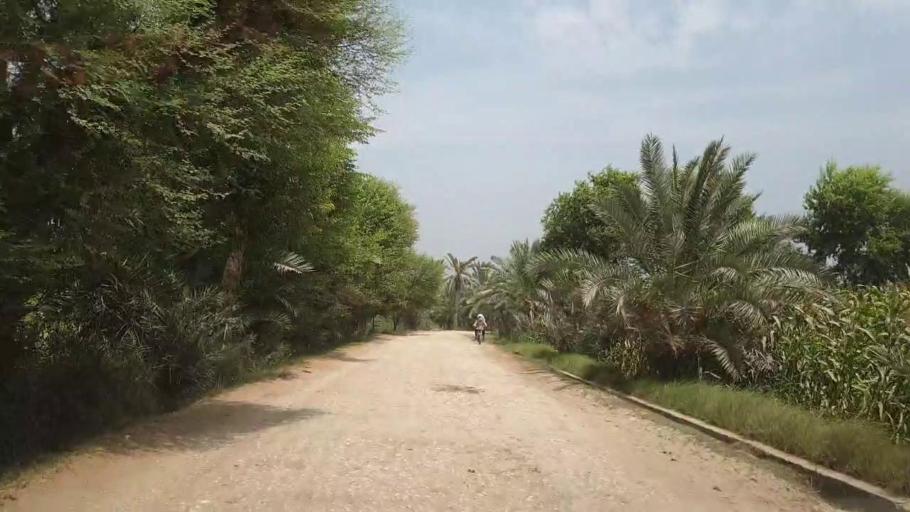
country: PK
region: Sindh
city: Pir jo Goth
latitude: 27.5191
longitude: 68.5782
